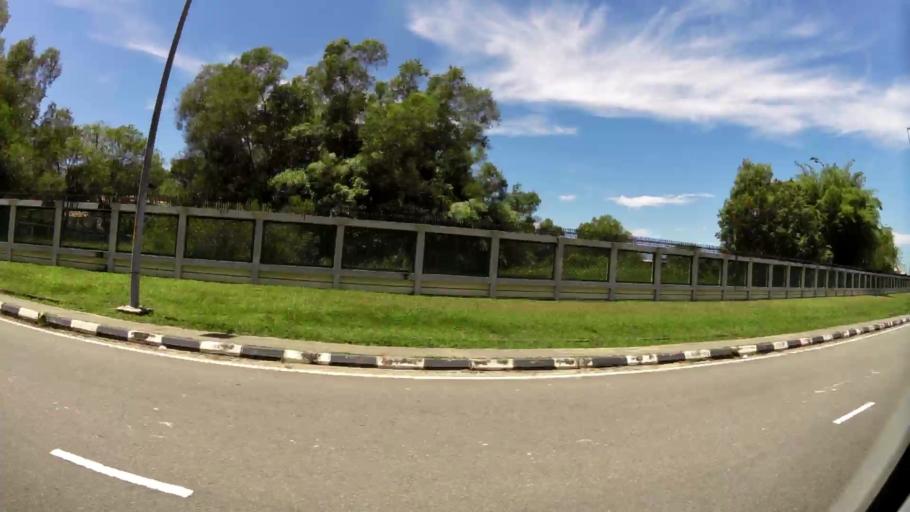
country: BN
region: Brunei and Muara
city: Bandar Seri Begawan
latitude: 4.9328
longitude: 114.9361
